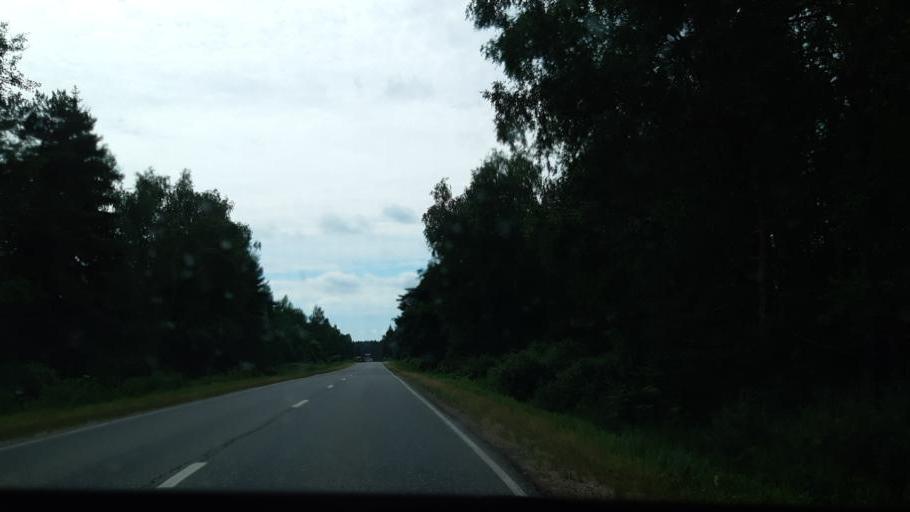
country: RU
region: Moskovskaya
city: Vereya
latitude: 55.3697
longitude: 36.2272
